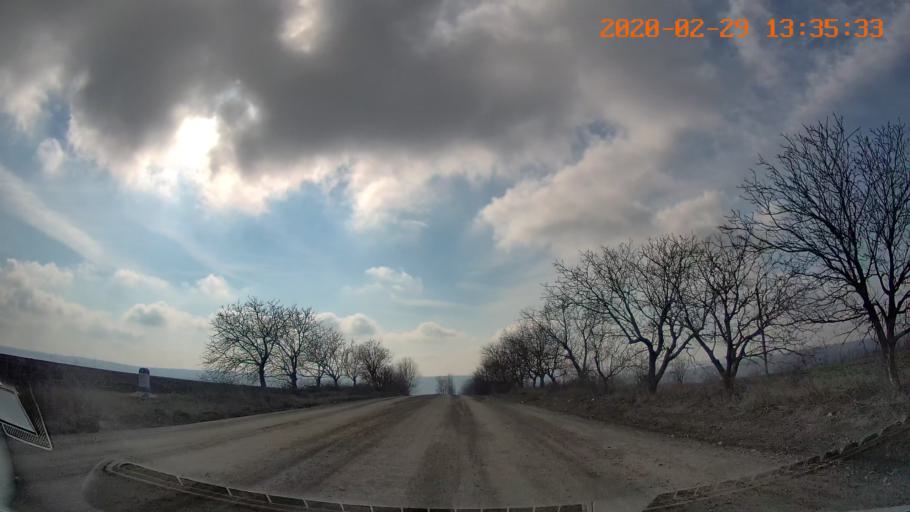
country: MD
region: Telenesti
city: Camenca
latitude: 47.8654
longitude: 28.6124
